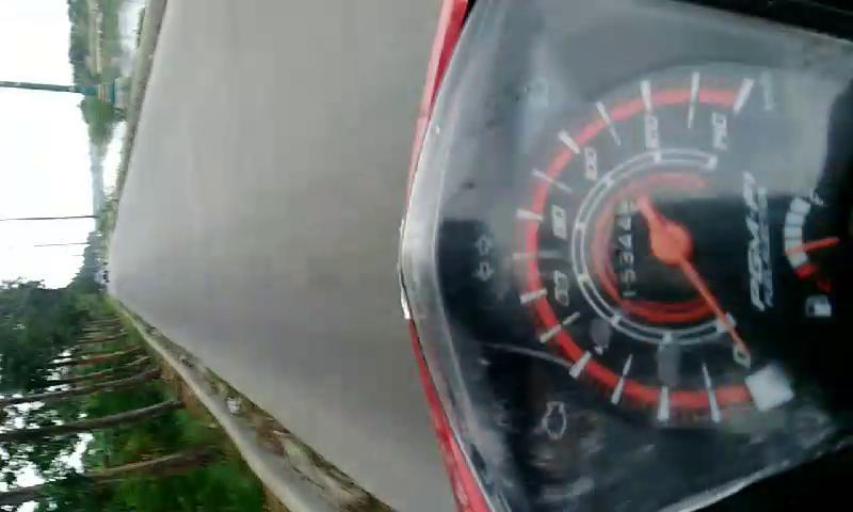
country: ID
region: West Java
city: Bekasi
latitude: -6.1586
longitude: 106.9713
